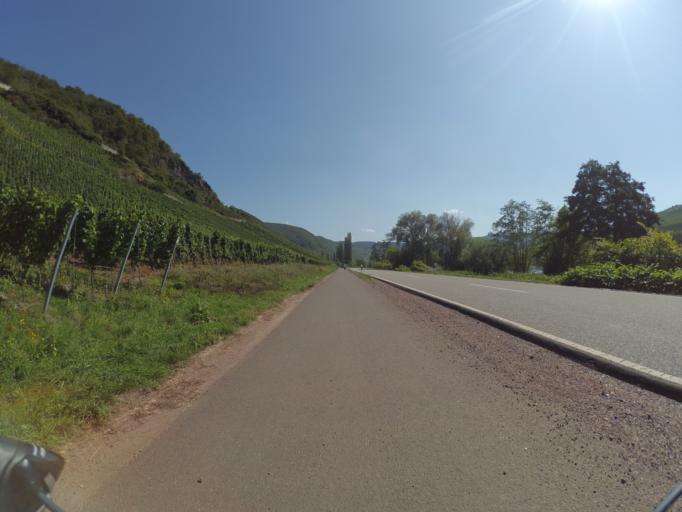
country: DE
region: Rheinland-Pfalz
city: Trittenheim
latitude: 49.8365
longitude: 6.8991
